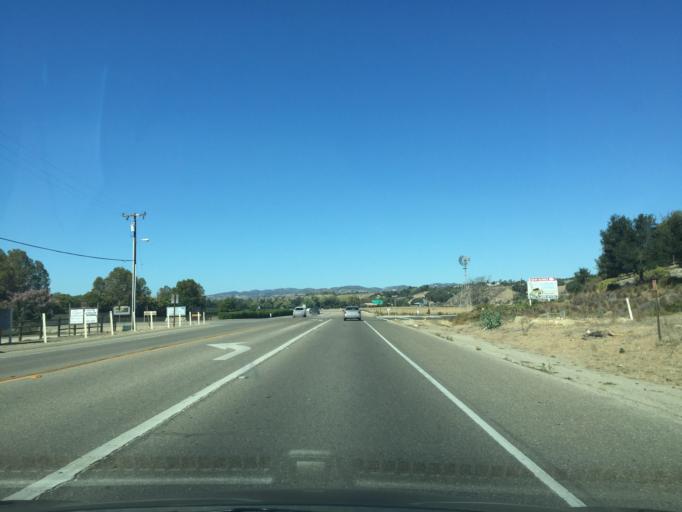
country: US
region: California
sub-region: Santa Barbara County
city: Solvang
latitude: 34.5953
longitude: -120.1539
